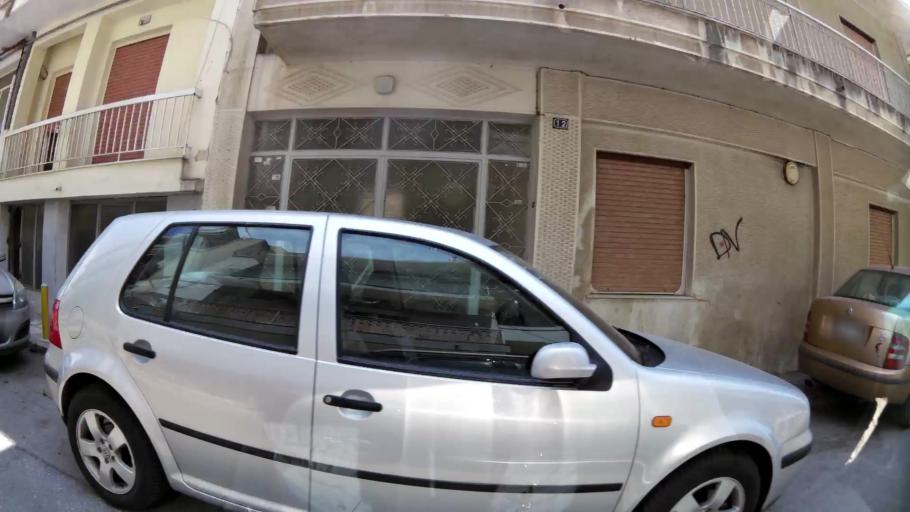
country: GR
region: Central Macedonia
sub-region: Nomos Thessalonikis
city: Ampelokipoi
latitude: 40.6505
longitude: 22.9328
